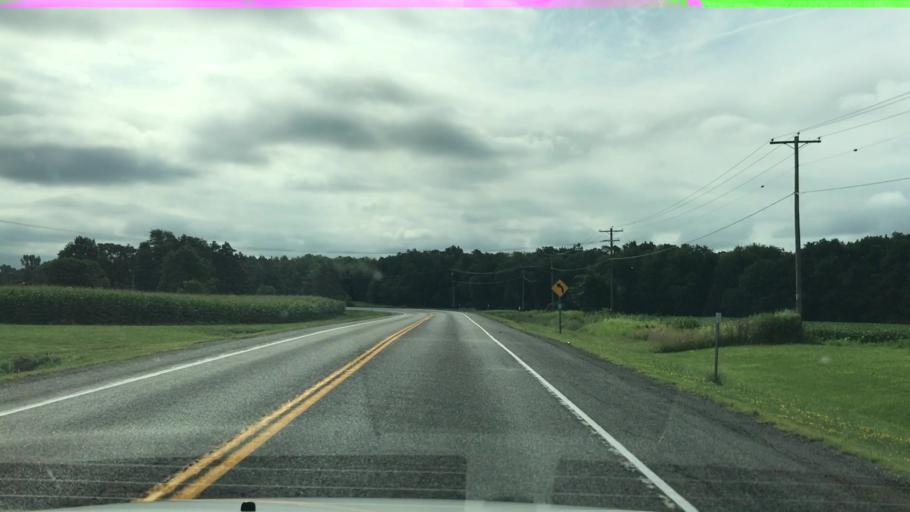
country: US
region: New York
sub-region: Erie County
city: Alden
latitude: 42.8359
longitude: -78.4508
